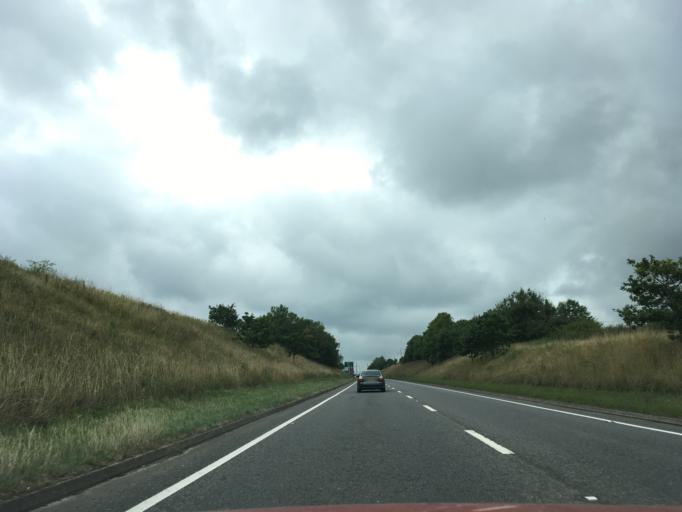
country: GB
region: Wales
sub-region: Carmarthenshire
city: Whitland
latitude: 51.8243
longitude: -4.5868
